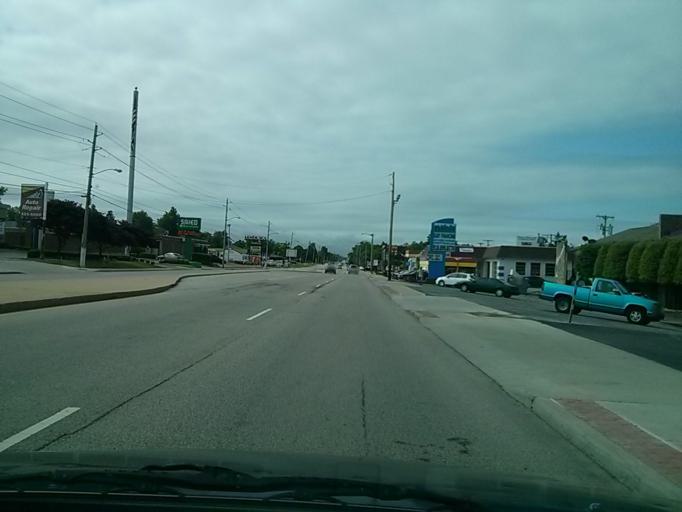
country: US
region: Oklahoma
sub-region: Tulsa County
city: Tulsa
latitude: 36.1168
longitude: -95.9225
